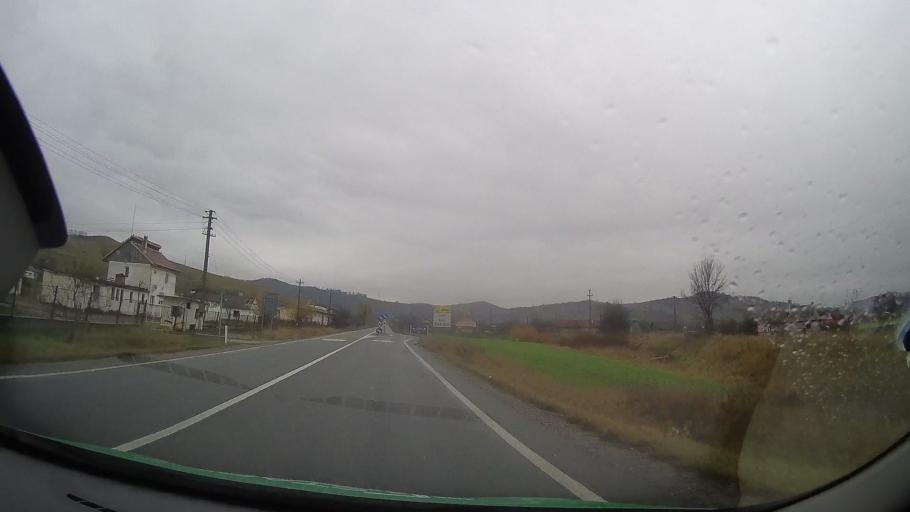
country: RO
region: Bistrita-Nasaud
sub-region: Comuna Teaca
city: Teaca
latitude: 46.9186
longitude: 24.4931
